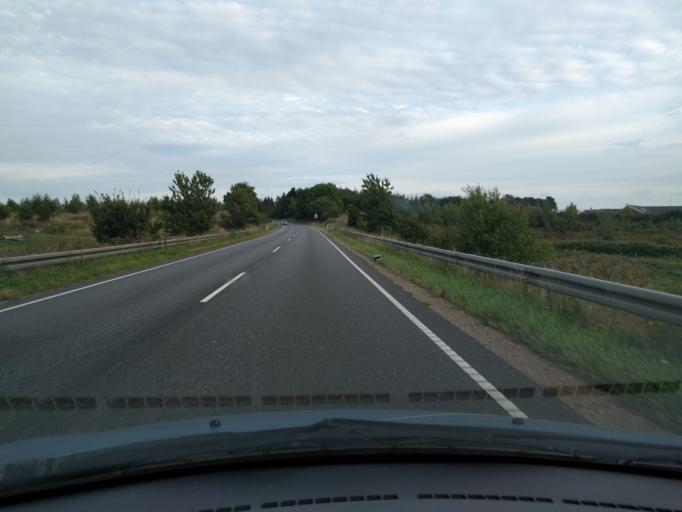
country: DK
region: Zealand
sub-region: Vordingborg Kommune
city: Nyrad
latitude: 55.0045
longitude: 11.9821
